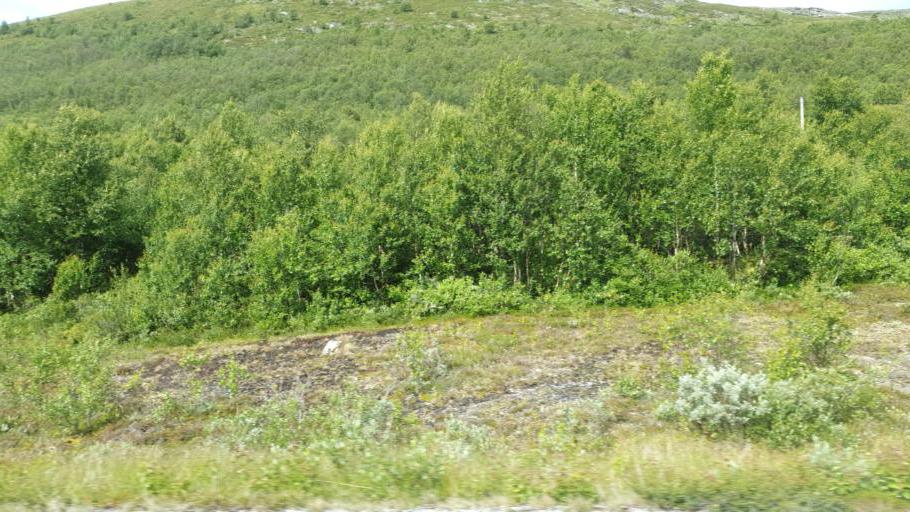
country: NO
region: Oppland
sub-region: Vaga
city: Vagamo
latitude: 61.5289
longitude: 8.8783
